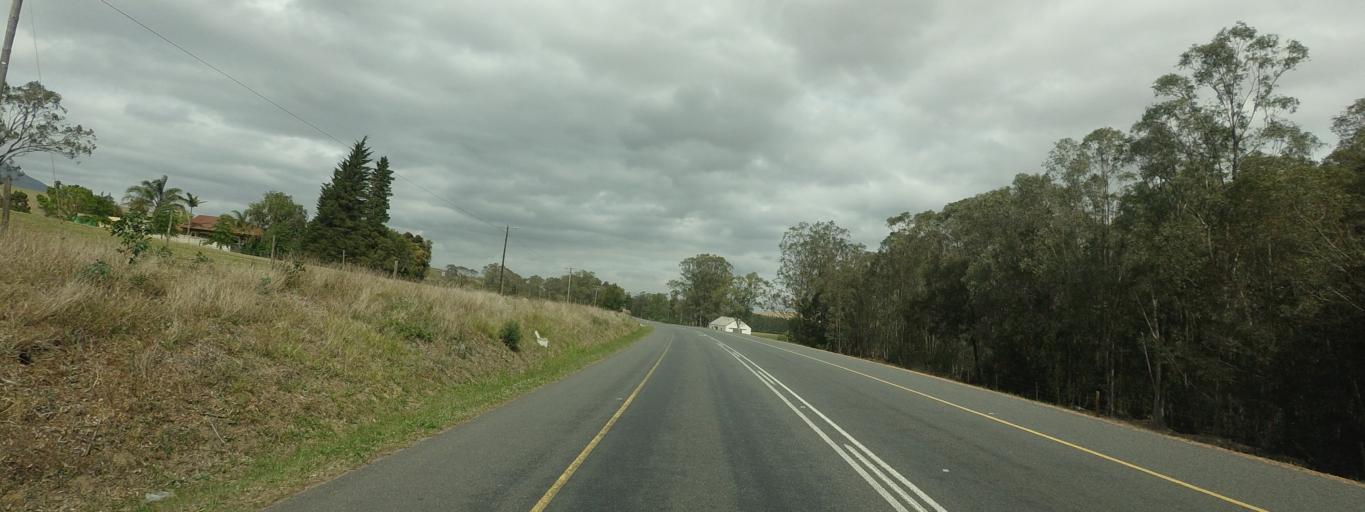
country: ZA
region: Western Cape
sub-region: Overberg District Municipality
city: Swellendam
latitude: -34.0131
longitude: 20.3937
